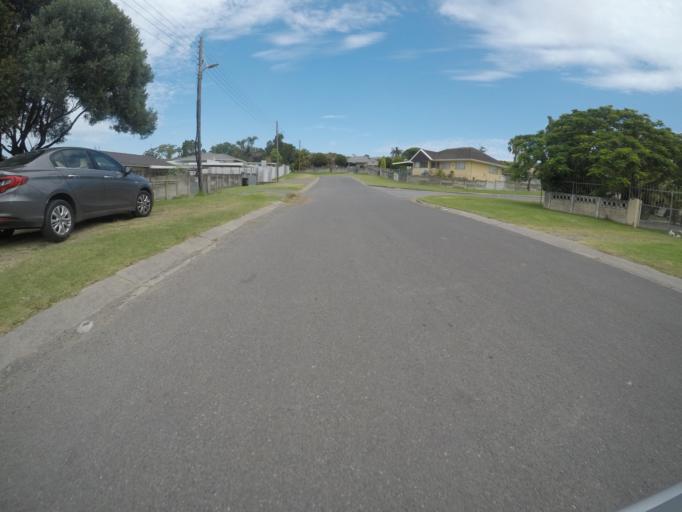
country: ZA
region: Eastern Cape
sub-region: Buffalo City Metropolitan Municipality
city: East London
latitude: -32.9936
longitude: 27.8735
